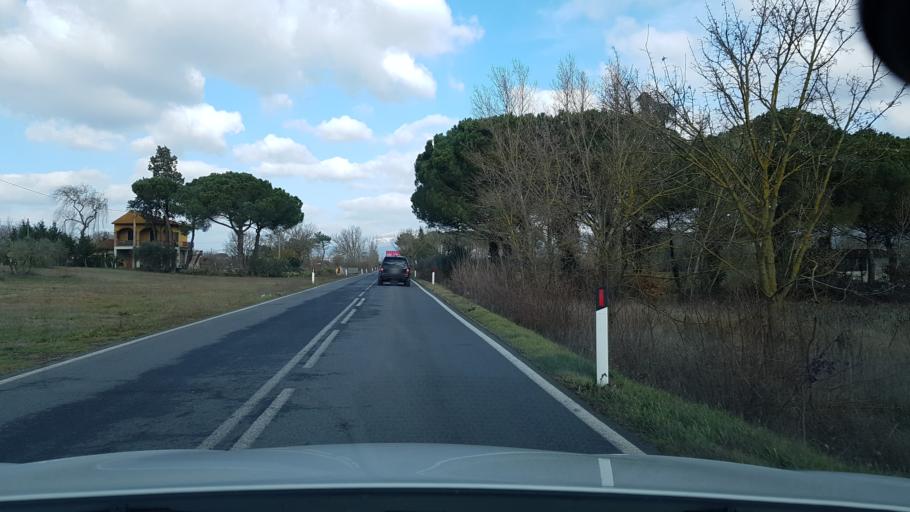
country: IT
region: Tuscany
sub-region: Province of Arezzo
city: Terontola
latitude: 43.1681
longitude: 12.0145
